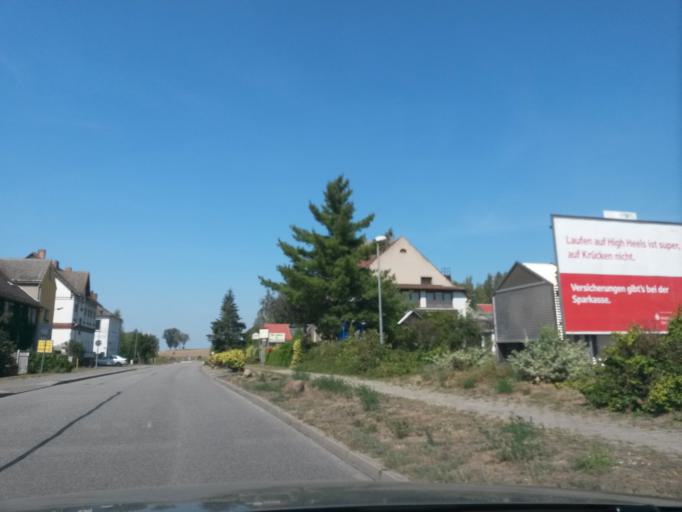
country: DE
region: Brandenburg
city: Gorzke
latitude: 52.1758
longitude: 12.3728
